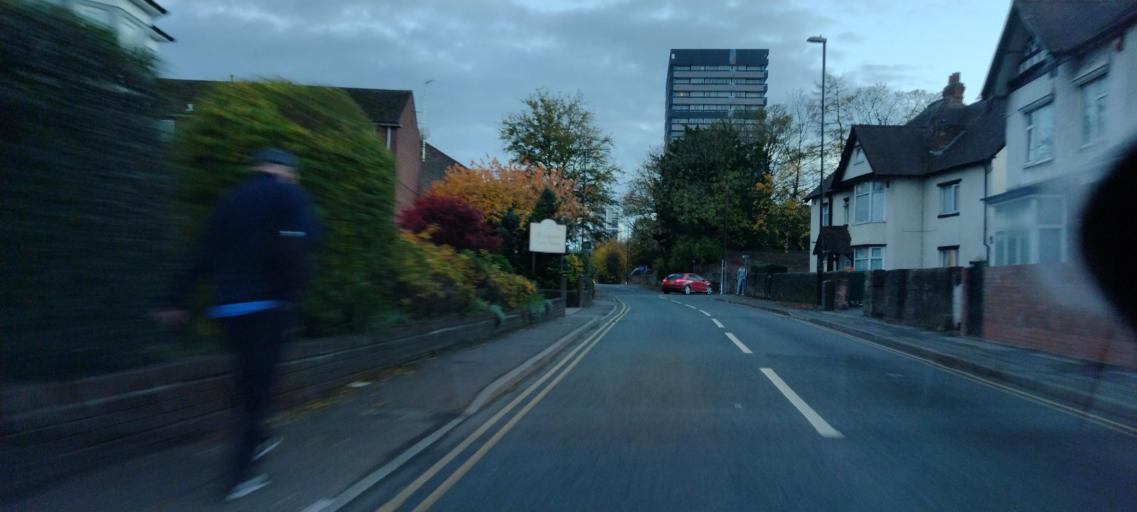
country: GB
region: England
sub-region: Coventry
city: Coventry
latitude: 52.4154
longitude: -1.5142
